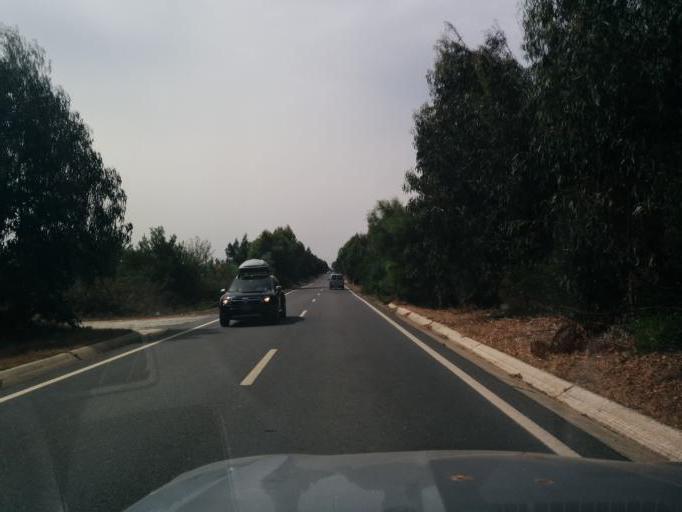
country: PT
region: Beja
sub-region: Odemira
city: Vila Nova de Milfontes
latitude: 37.6675
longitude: -8.7596
